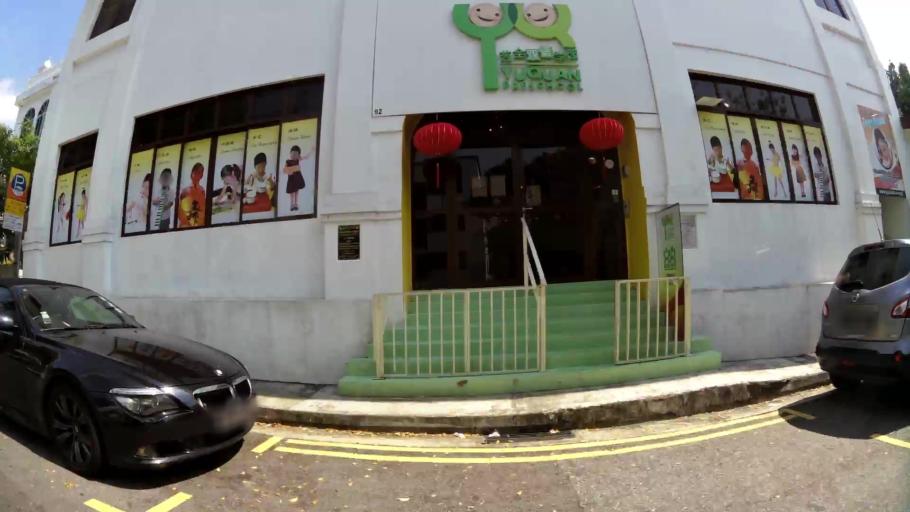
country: SG
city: Singapore
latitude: 1.3035
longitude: 103.8470
